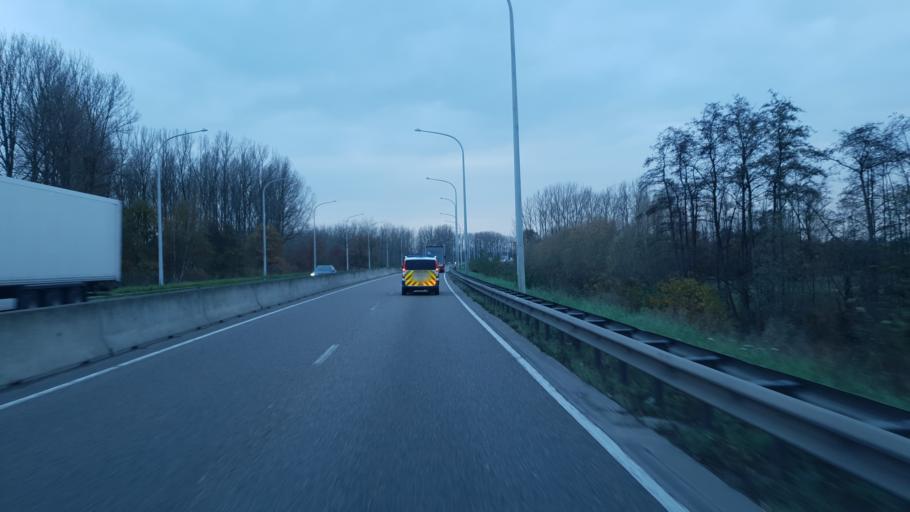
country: BE
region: Flanders
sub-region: Provincie Limburg
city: Diepenbeek
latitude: 50.9132
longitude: 5.4380
